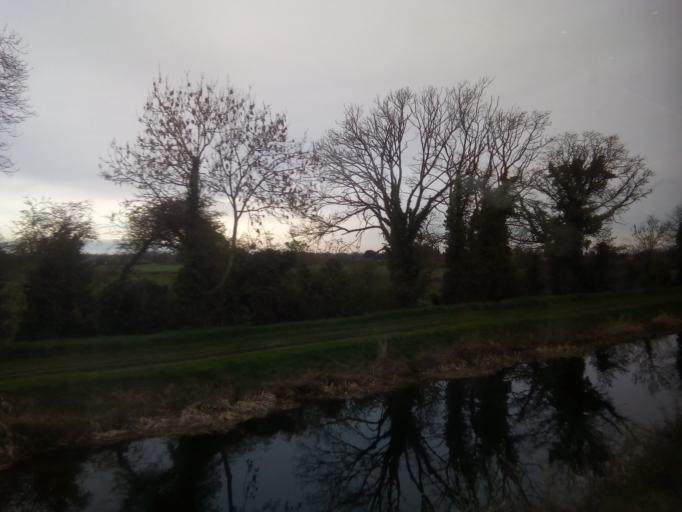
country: IE
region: Leinster
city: Lucan
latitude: 53.3795
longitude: -6.4464
